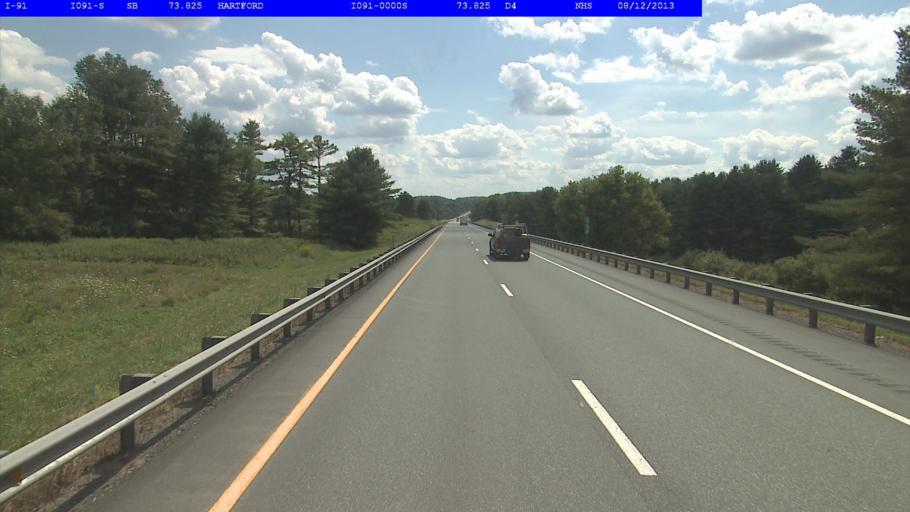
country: US
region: Vermont
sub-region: Windsor County
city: Wilder
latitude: 43.6922
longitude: -72.3118
